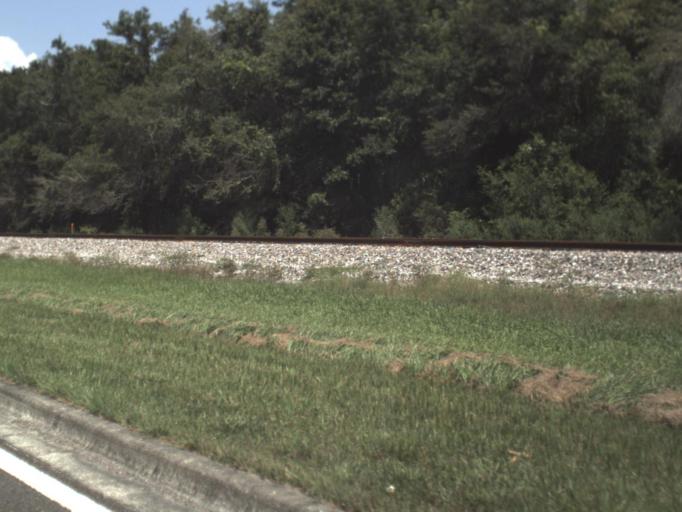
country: US
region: Florida
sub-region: Hillsborough County
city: Lake Magdalene
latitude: 28.1082
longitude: -82.4589
